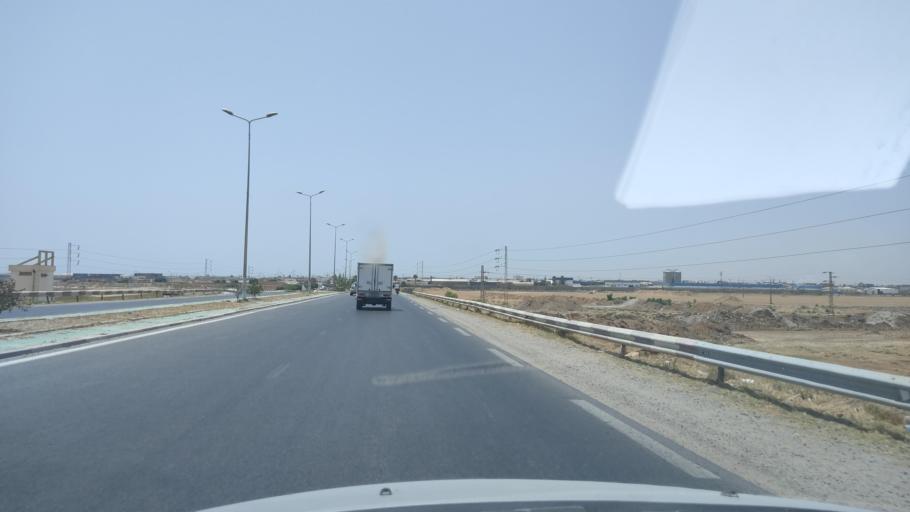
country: TN
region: Safaqis
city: Sfax
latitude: 34.7045
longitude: 10.7206
